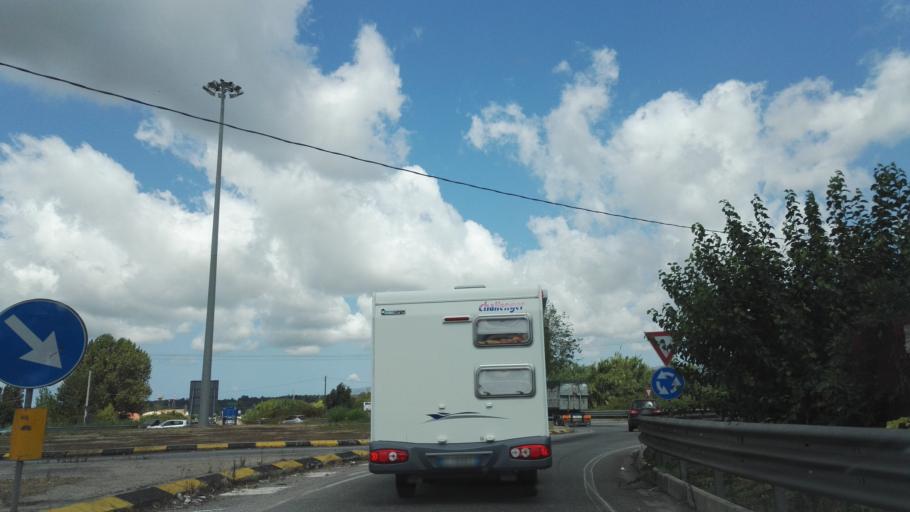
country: IT
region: Calabria
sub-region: Provincia di Reggio Calabria
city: Rosarno
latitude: 38.4660
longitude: 16.0106
